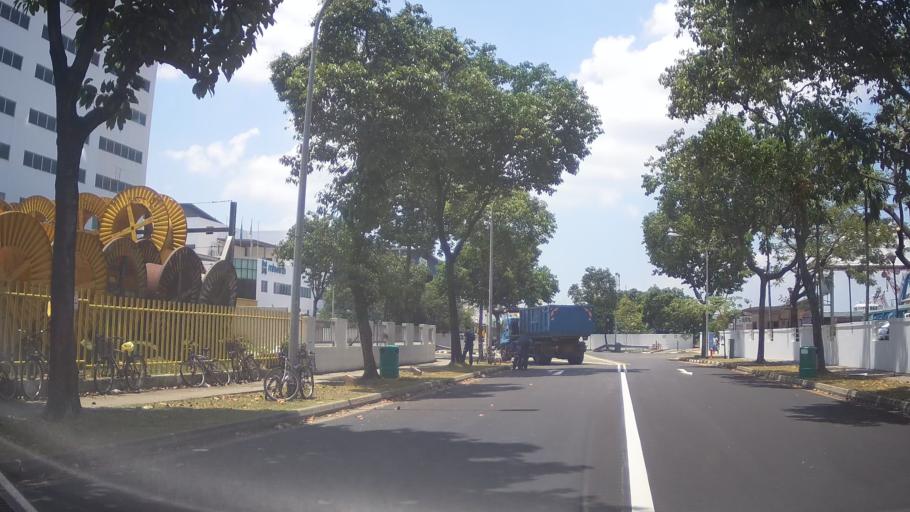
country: SG
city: Singapore
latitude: 1.3050
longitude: 103.6744
